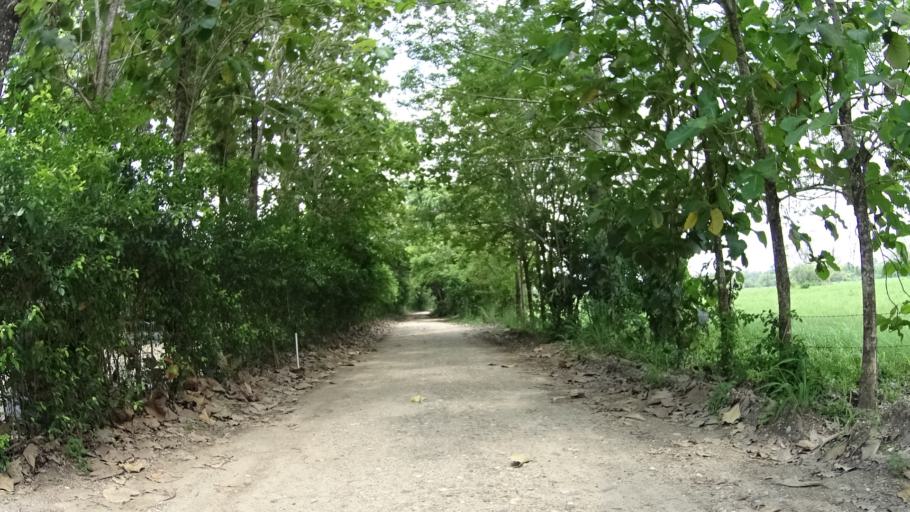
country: CO
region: Cundinamarca
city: Puerto Salgar
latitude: 5.5400
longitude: -74.6757
